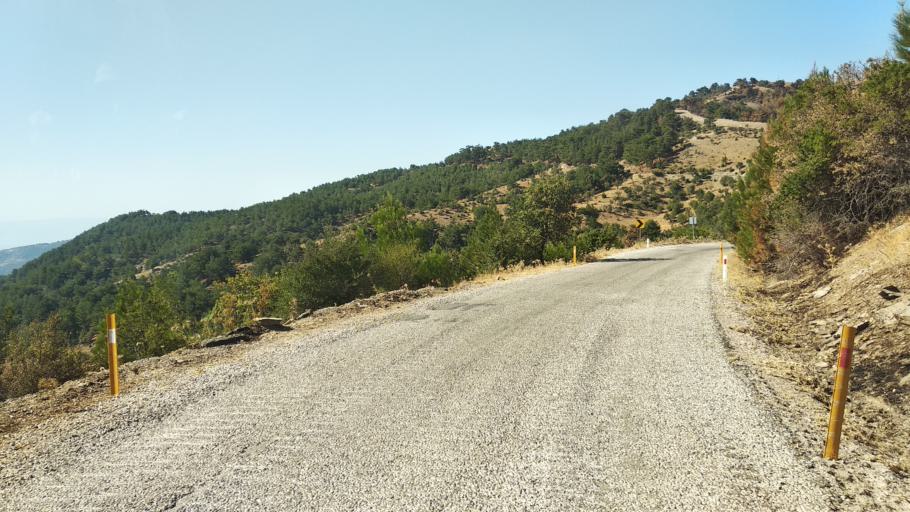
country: TR
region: Izmir
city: Gaziemir
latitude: 38.2914
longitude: 27.0010
